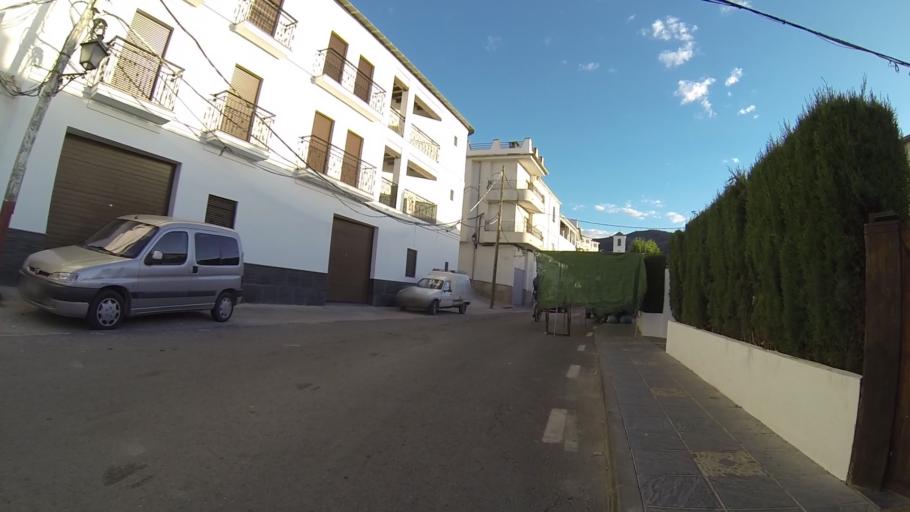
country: ES
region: Andalusia
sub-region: Provincia de Granada
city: Berchules
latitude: 36.9812
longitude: -3.1559
